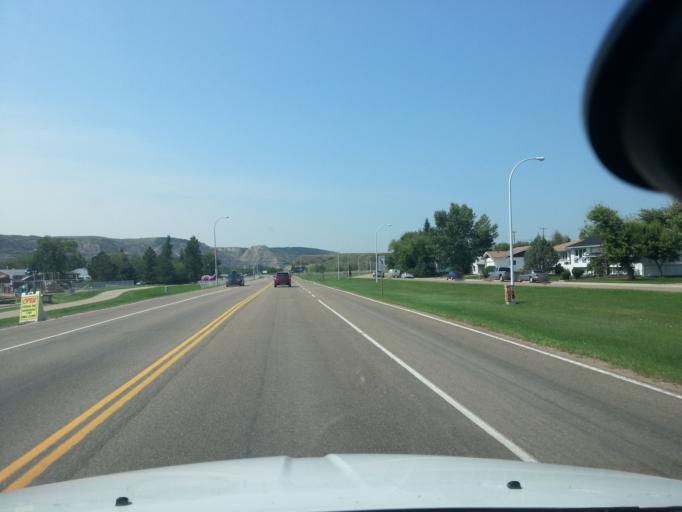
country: CA
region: Alberta
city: Three Hills
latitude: 51.4694
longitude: -112.7427
